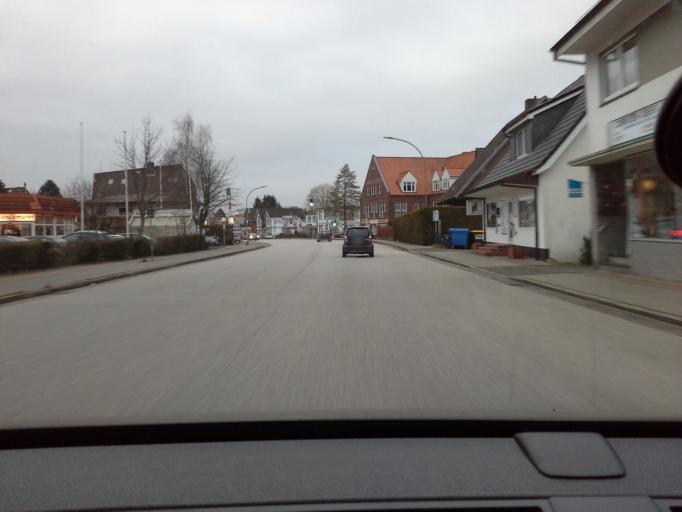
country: DE
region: Schleswig-Holstein
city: Quickborn
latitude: 53.7277
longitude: 9.8984
